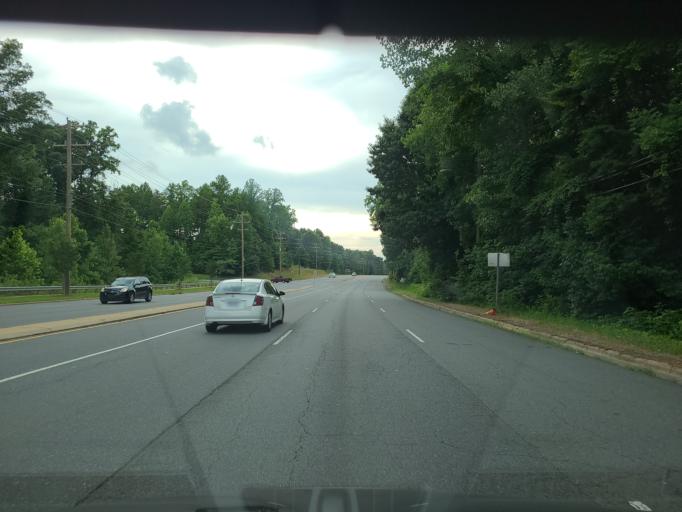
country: US
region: North Carolina
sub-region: Gaston County
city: Belmont
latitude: 35.2356
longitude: -80.9505
